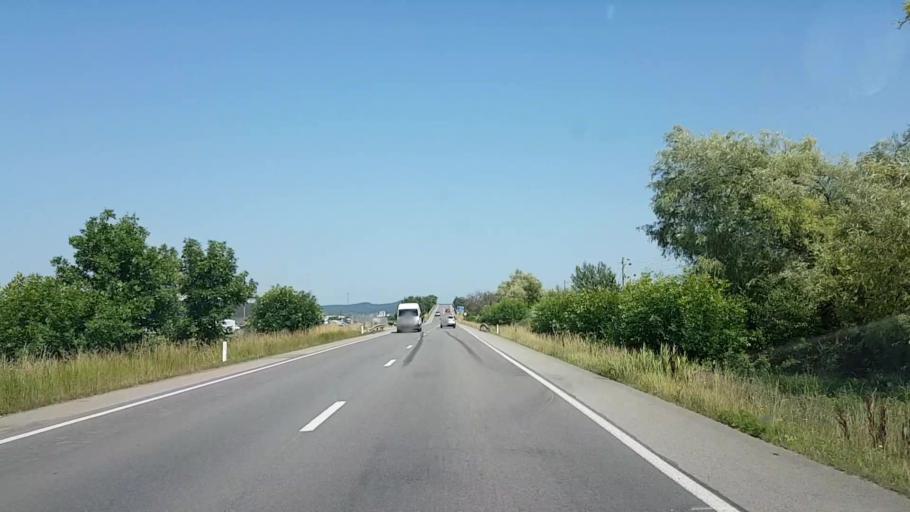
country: RO
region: Bistrita-Nasaud
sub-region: Comuna Sintereag
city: Cociu
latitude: 47.1832
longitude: 24.2255
